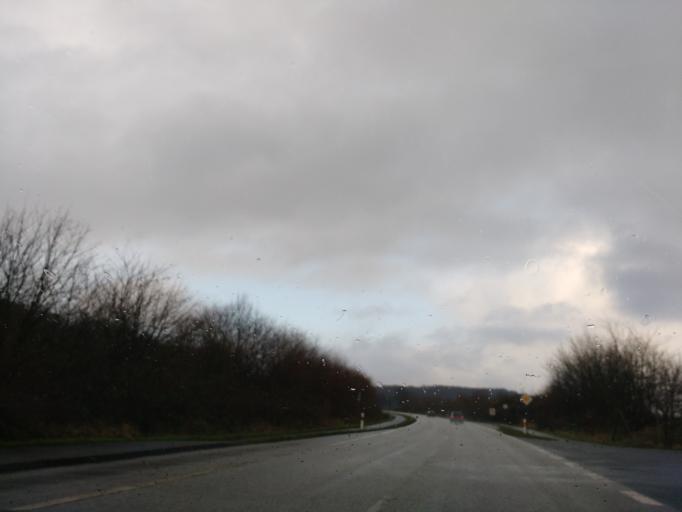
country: DE
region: Schleswig-Holstein
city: Gross Wittensee
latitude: 54.4115
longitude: 9.7903
